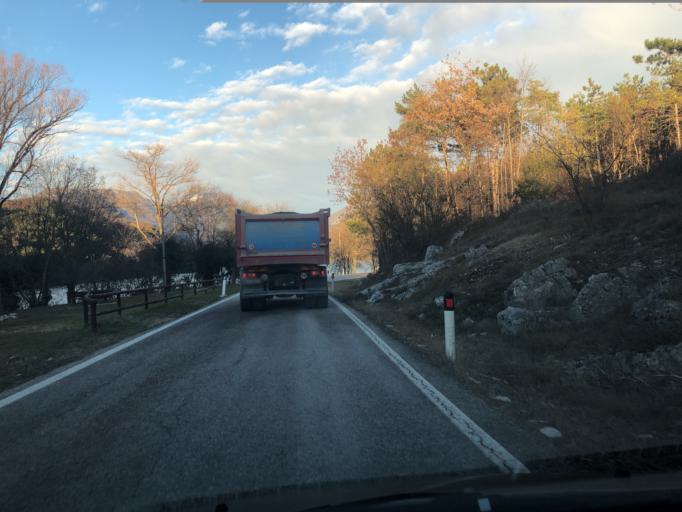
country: IT
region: Trentino-Alto Adige
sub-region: Provincia di Trento
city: Drena
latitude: 45.9918
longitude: 10.9431
